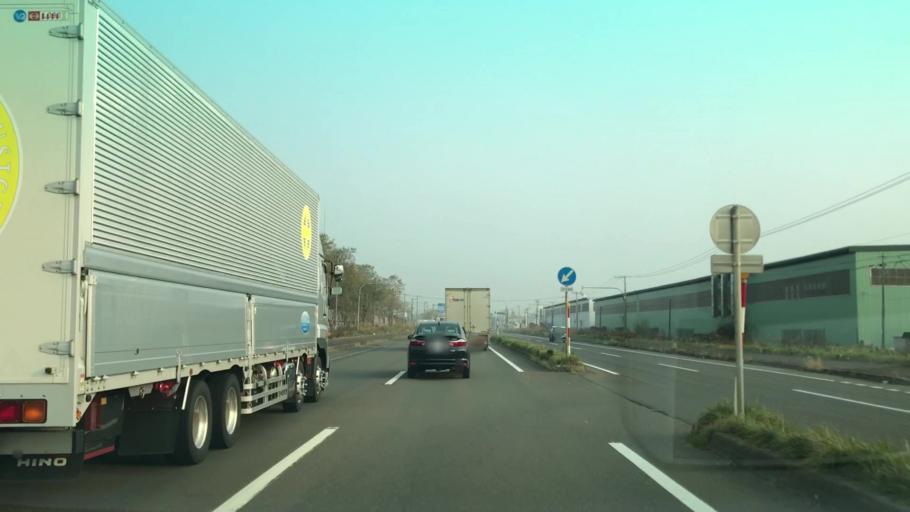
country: JP
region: Hokkaido
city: Ishikari
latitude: 43.1911
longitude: 141.3262
